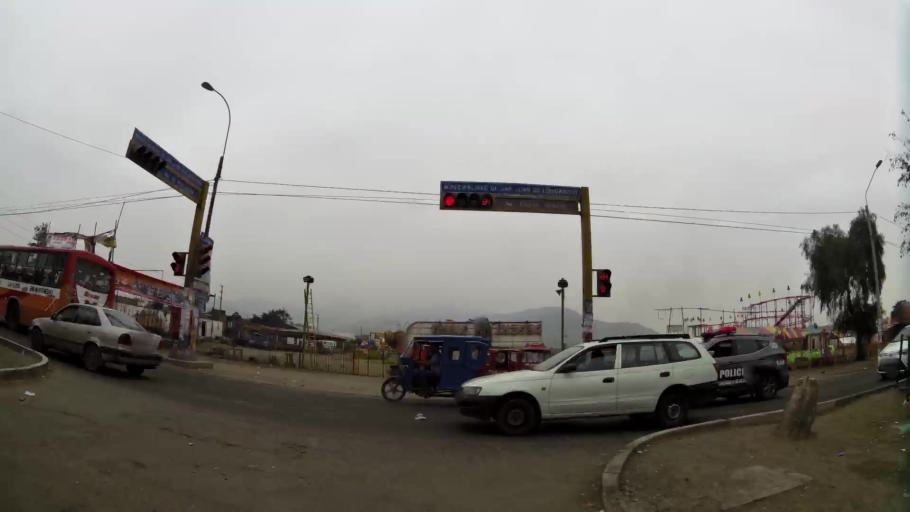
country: PE
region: Lima
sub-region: Lima
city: Independencia
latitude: -11.9754
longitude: -77.0089
